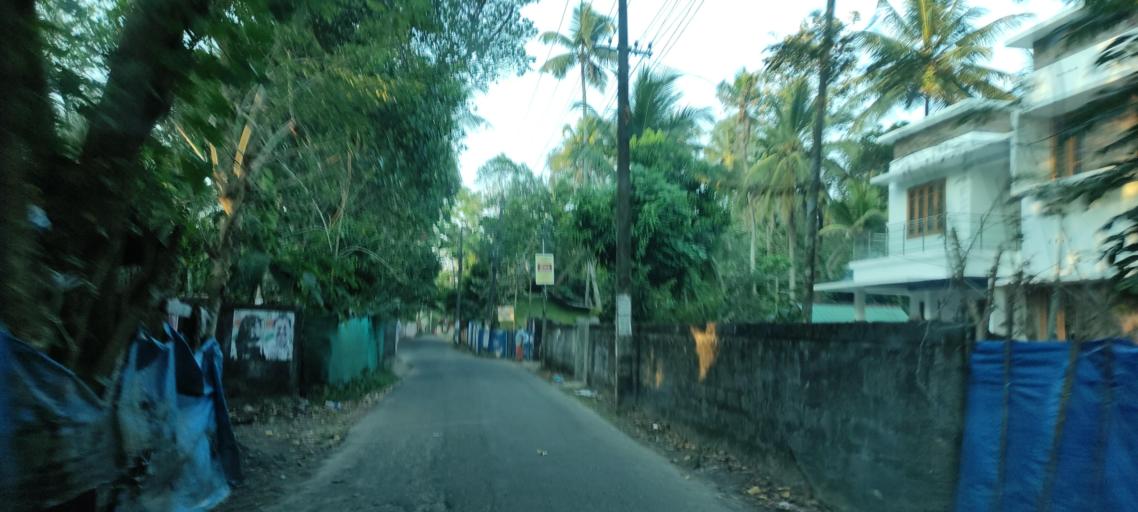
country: IN
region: Kerala
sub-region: Alappuzha
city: Kutiatodu
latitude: 9.7860
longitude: 76.3240
